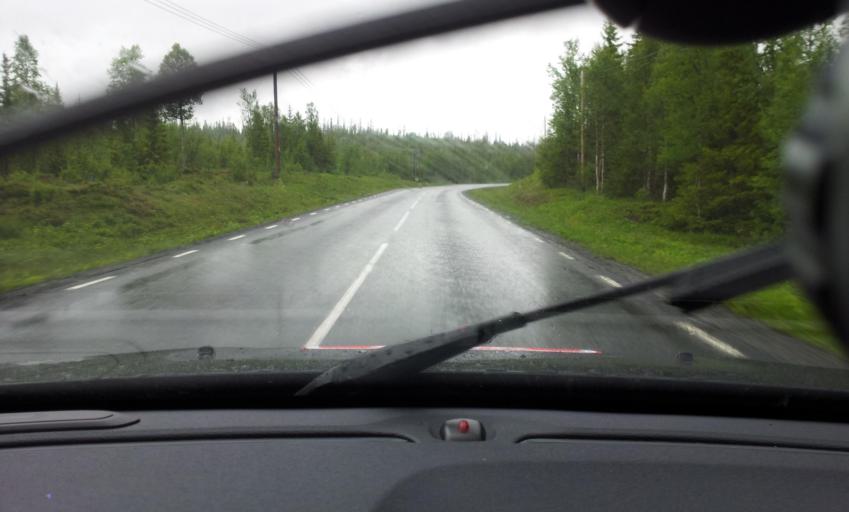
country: SE
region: Jaemtland
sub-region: Are Kommun
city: Are
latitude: 63.2422
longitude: 13.1790
